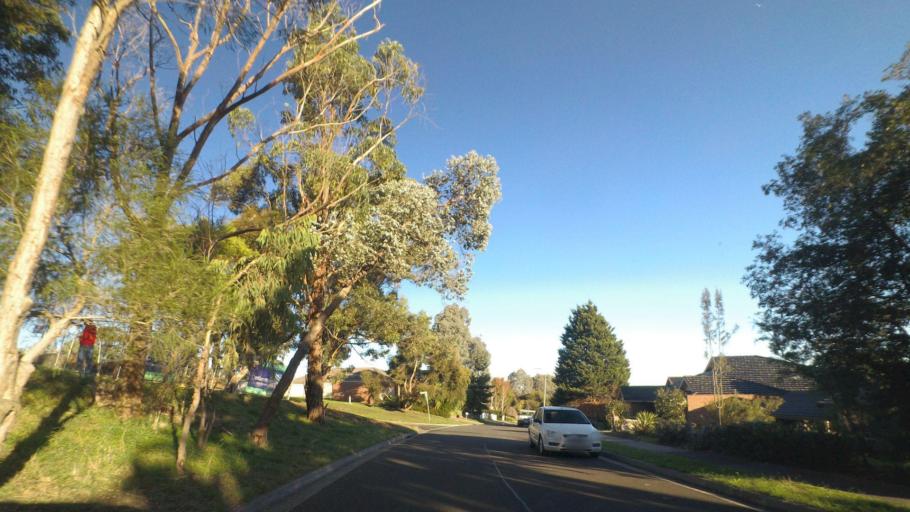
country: AU
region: Victoria
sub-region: Banyule
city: Greensborough
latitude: -37.6888
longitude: 145.1072
